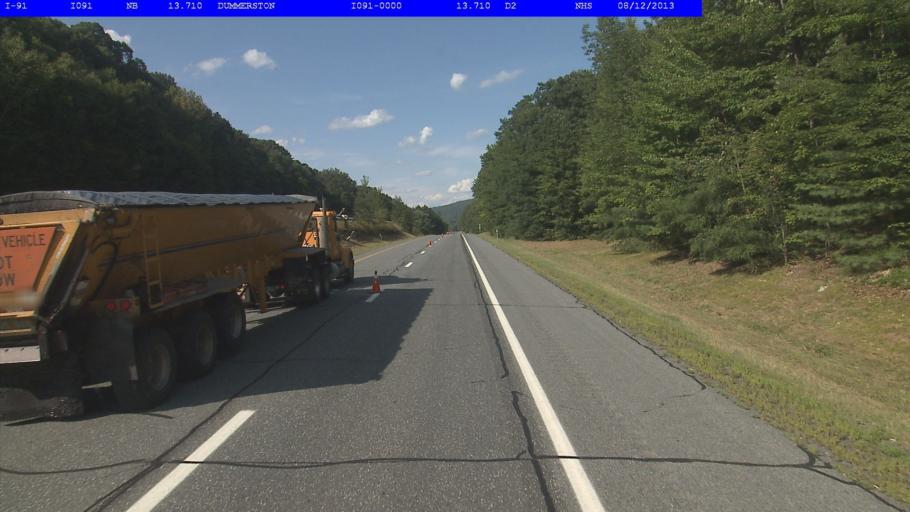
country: US
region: Vermont
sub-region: Windham County
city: Brattleboro
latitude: 42.9085
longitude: -72.5332
